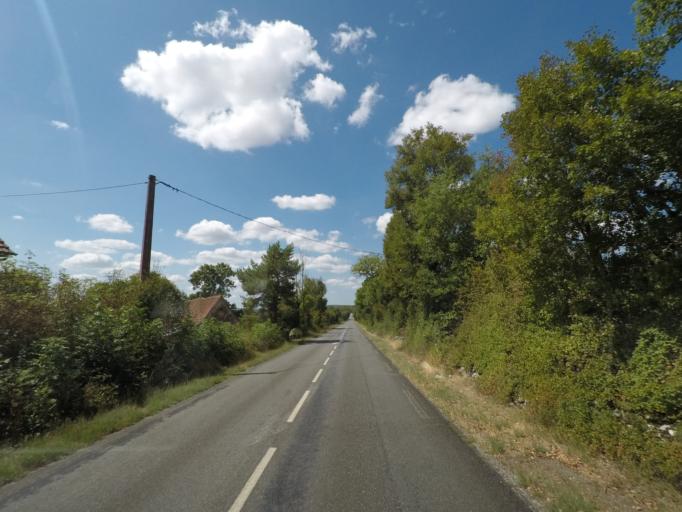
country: FR
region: Midi-Pyrenees
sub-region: Departement du Lot
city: Lacapelle-Marival
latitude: 44.6263
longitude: 1.8460
